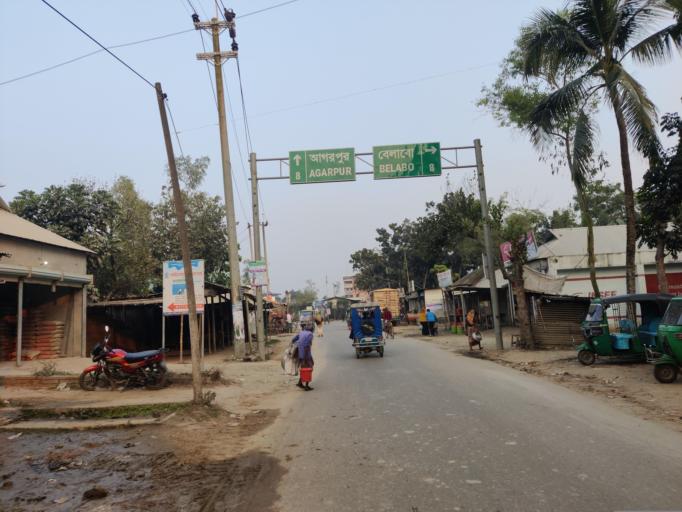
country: BD
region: Dhaka
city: Bajitpur
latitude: 24.1585
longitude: 90.8067
